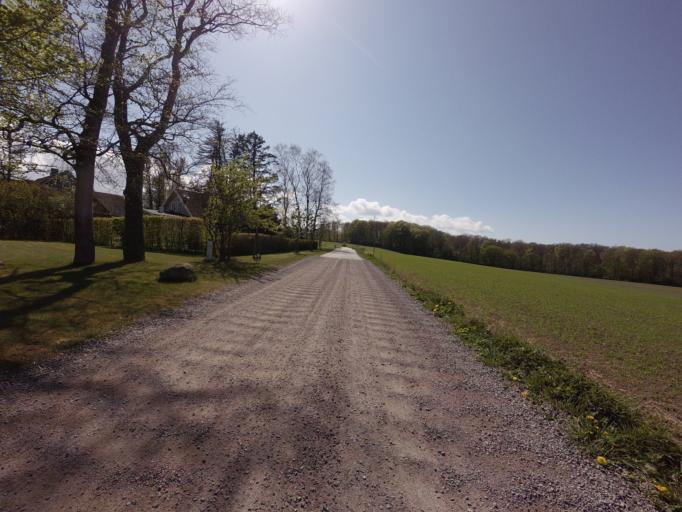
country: DK
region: Capital Region
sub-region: Helsingor Kommune
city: Hellebaek
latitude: 56.1255
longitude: 12.6219
